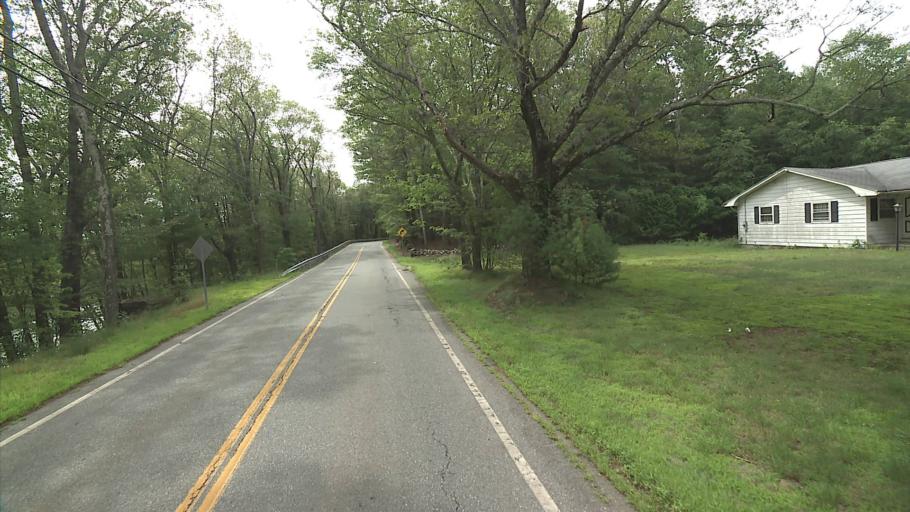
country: US
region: Massachusetts
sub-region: Worcester County
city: Webster
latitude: 42.0132
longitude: -71.8446
